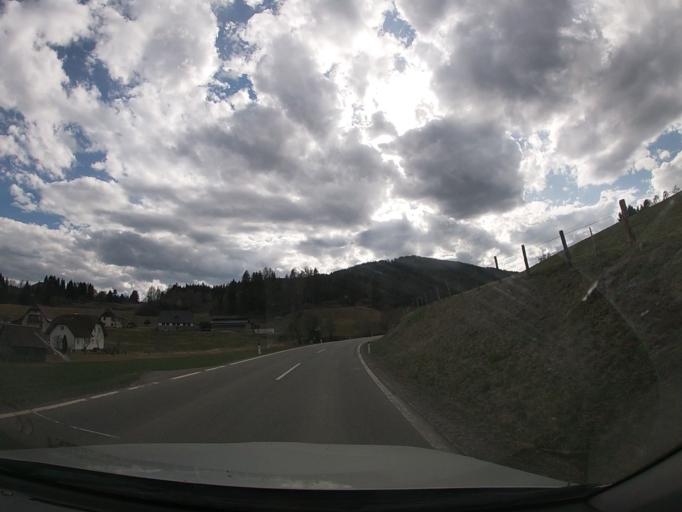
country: AT
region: Styria
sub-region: Politischer Bezirk Murau
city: Sankt Lambrecht
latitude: 47.0633
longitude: 14.2910
